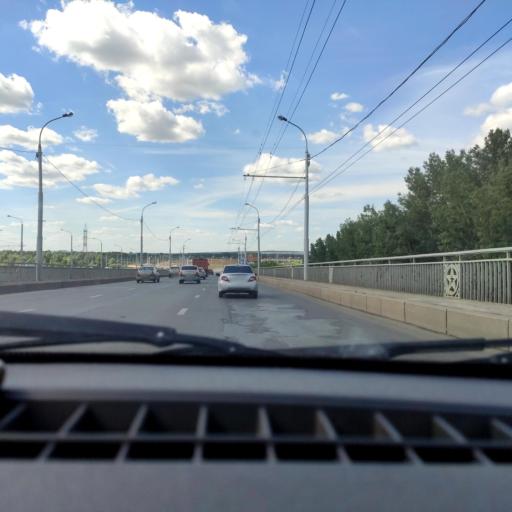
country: RU
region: Bashkortostan
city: Ufa
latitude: 54.7596
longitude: 55.9639
